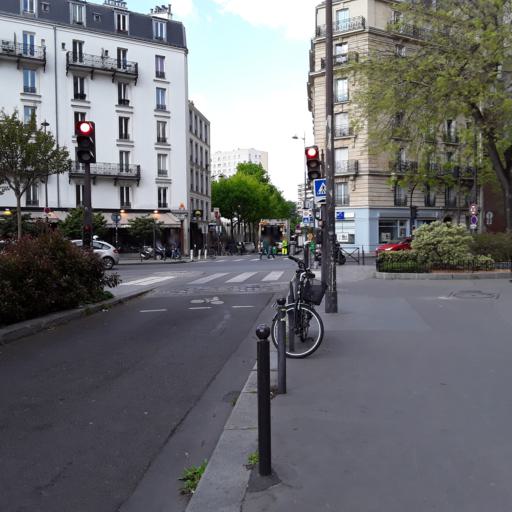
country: FR
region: Ile-de-France
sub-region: Departement du Val-de-Marne
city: Le Kremlin-Bicetre
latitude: 48.8263
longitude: 2.3636
